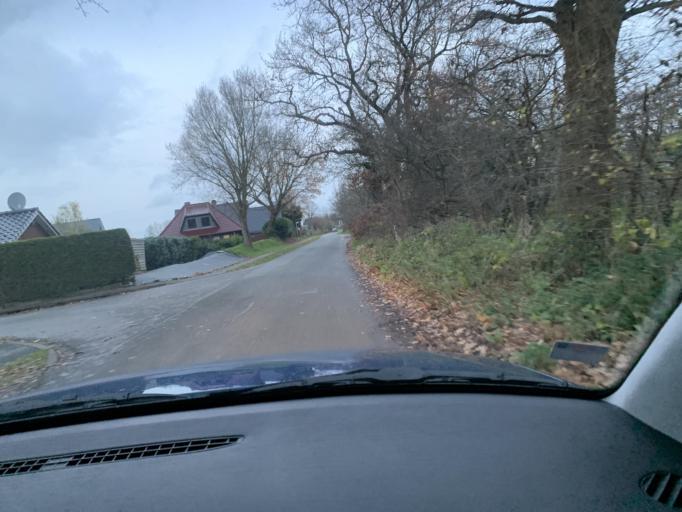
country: DE
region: Schleswig-Holstein
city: Wesseln
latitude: 54.2046
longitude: 9.0756
